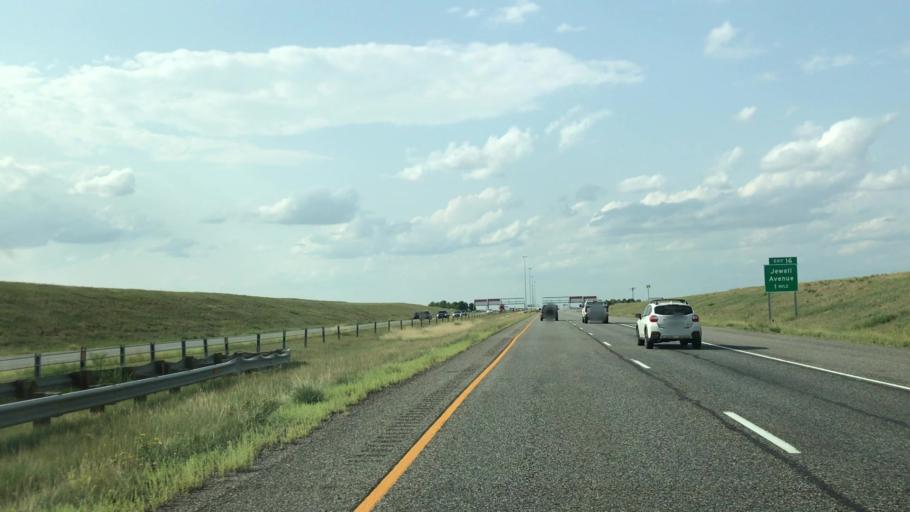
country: US
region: Colorado
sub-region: Adams County
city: Aurora
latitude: 39.6621
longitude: -104.7217
